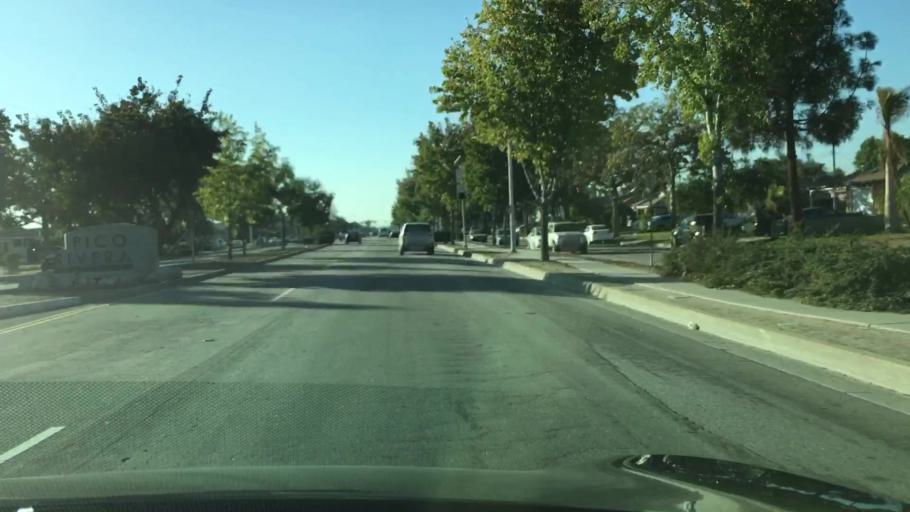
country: US
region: California
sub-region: Los Angeles County
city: Pico Rivera
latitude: 33.9771
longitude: -118.0858
